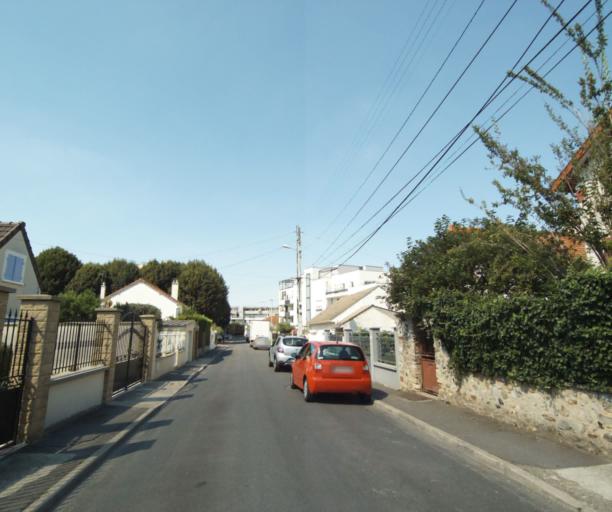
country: FR
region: Ile-de-France
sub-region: Departement de Seine-et-Marne
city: Pomponne
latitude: 48.8769
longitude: 2.6939
